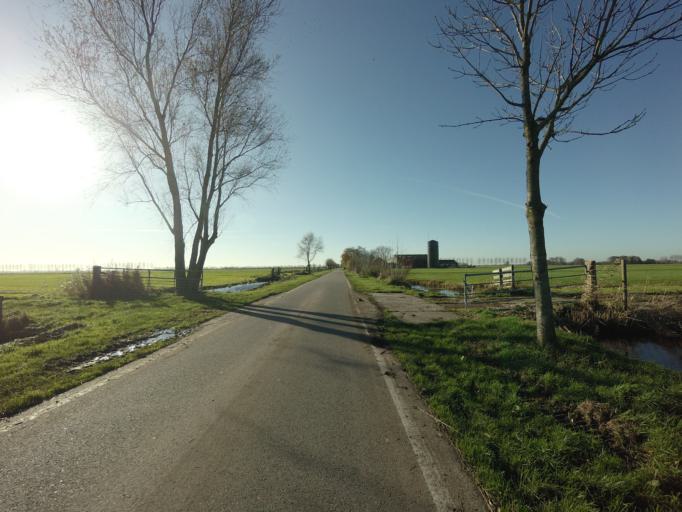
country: NL
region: South Holland
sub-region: Gemeente Nieuwkoop
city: Nieuwkoop
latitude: 52.1191
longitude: 4.8160
